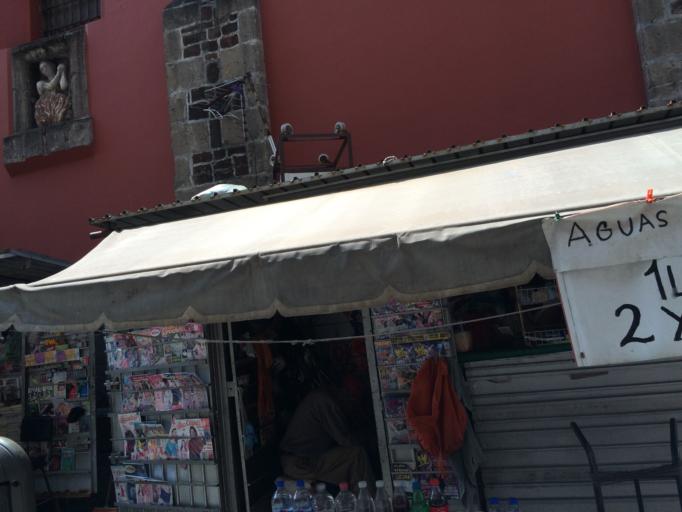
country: MX
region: Mexico City
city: Mexico City
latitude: 19.4350
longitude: -99.1334
